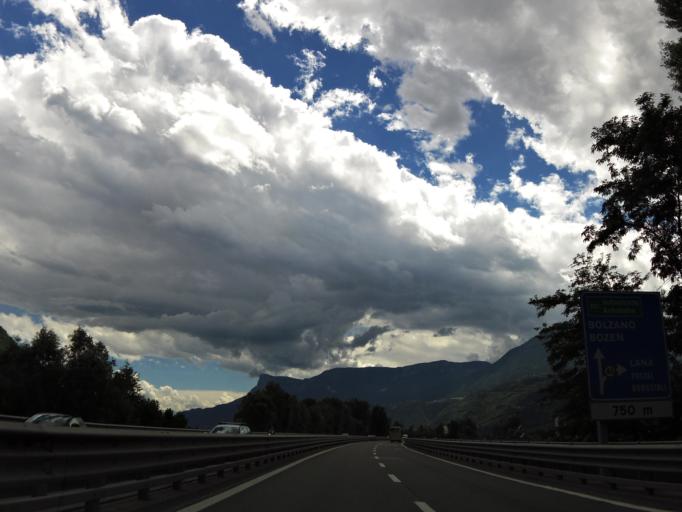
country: IT
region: Trentino-Alto Adige
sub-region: Bolzano
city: Postal
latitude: 46.6182
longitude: 11.1838
